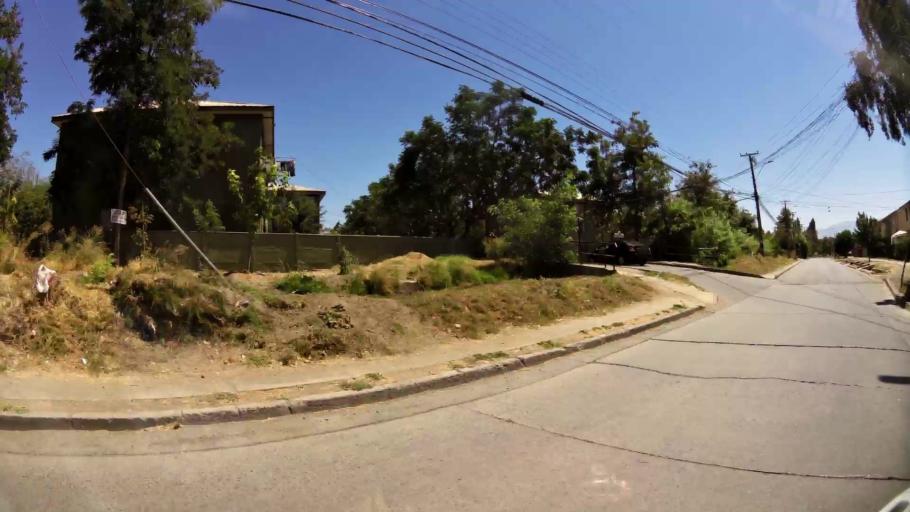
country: CL
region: O'Higgins
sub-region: Provincia de Cachapoal
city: Rancagua
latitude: -34.1558
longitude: -70.7503
